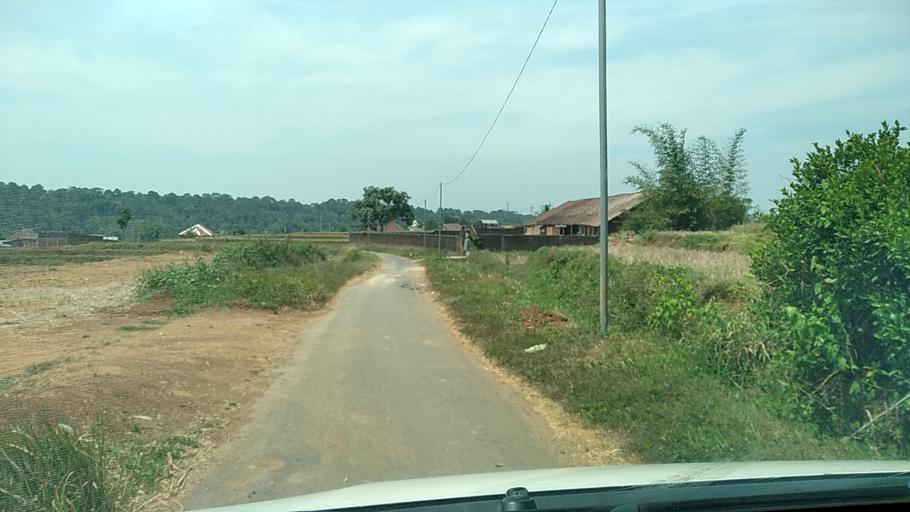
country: ID
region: Central Java
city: Ungaran
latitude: -7.0825
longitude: 110.3264
